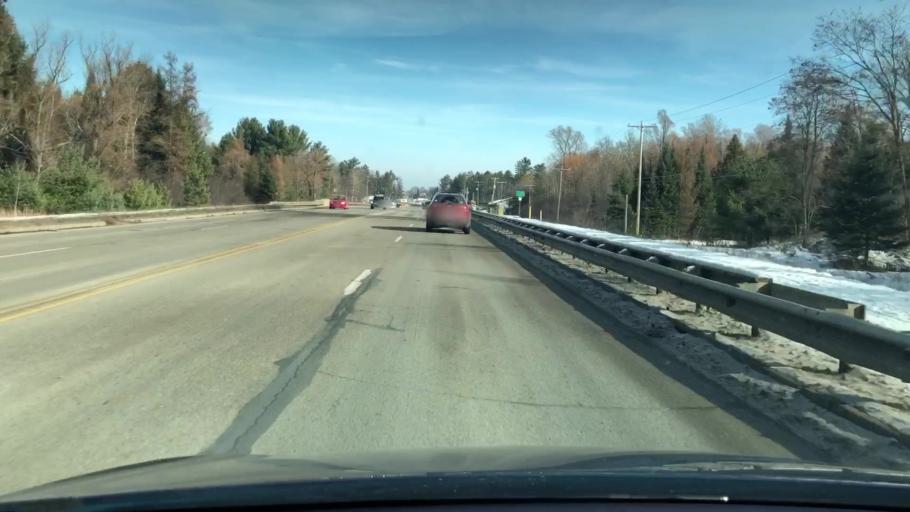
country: US
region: Michigan
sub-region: Crawford County
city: Grayling
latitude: 44.6572
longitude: -84.7271
